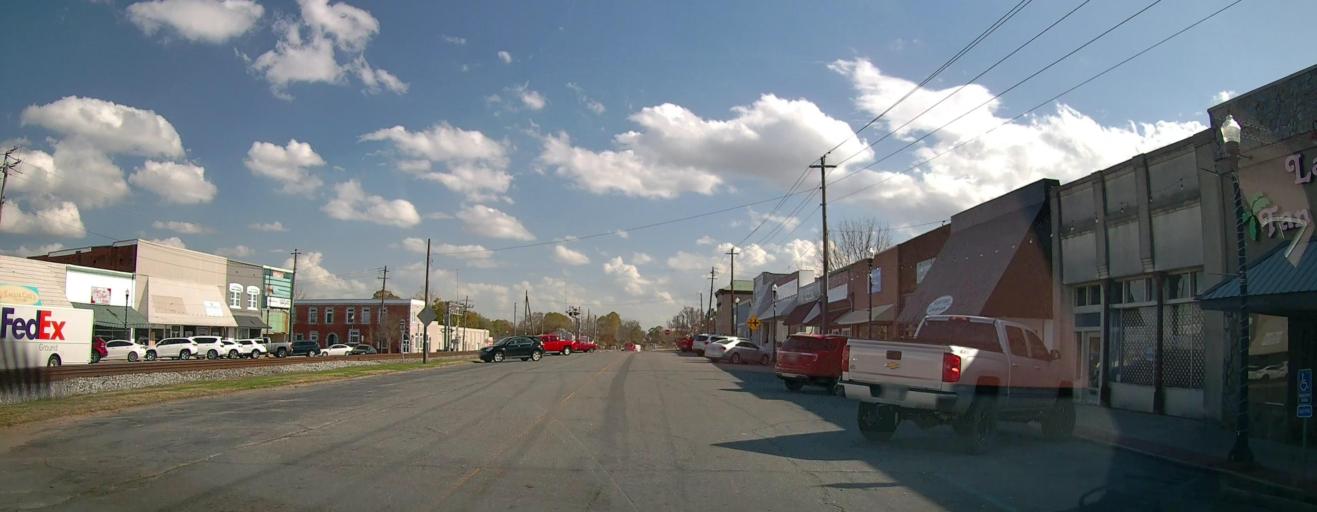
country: US
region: Georgia
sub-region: Dodge County
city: Eastman
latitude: 32.1978
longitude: -83.1761
